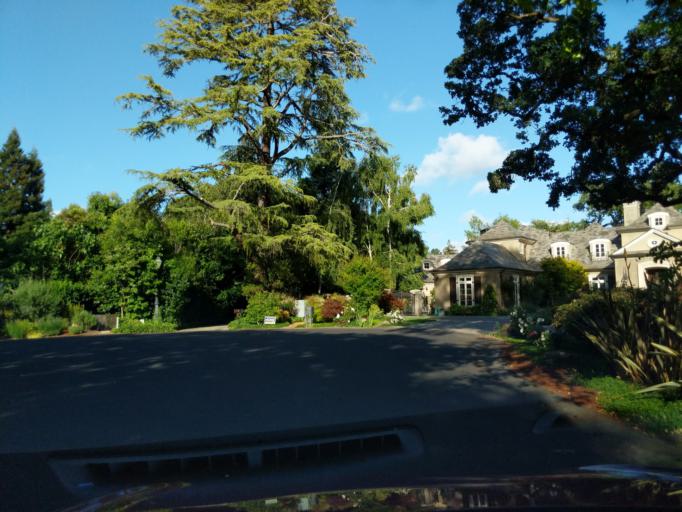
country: US
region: California
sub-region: San Mateo County
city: West Menlo Park
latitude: 37.4446
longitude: -122.1949
